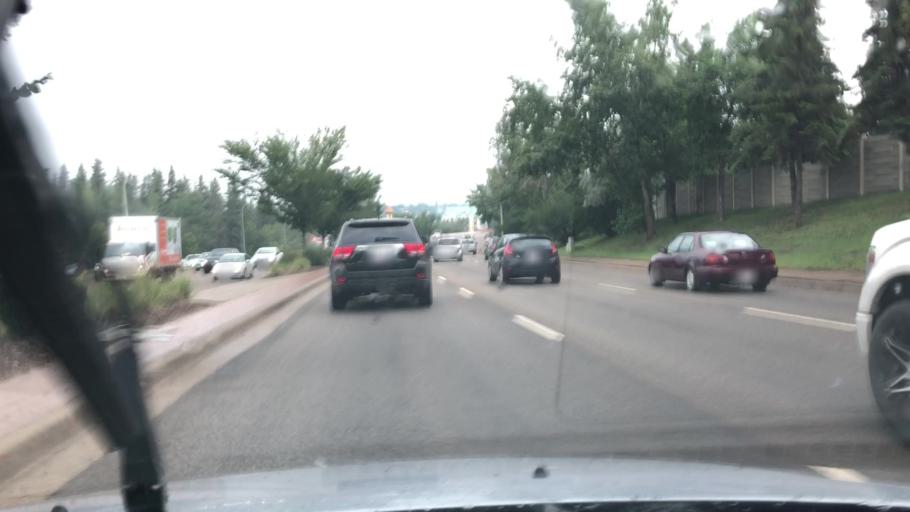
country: CA
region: Alberta
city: St. Albert
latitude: 53.6293
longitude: -113.6205
